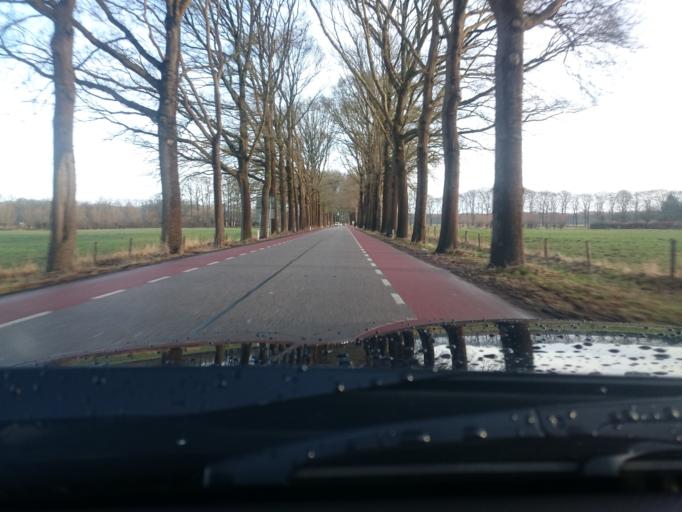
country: NL
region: Gelderland
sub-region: Gemeente Voorst
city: Voorst
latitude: 52.1934
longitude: 6.1297
